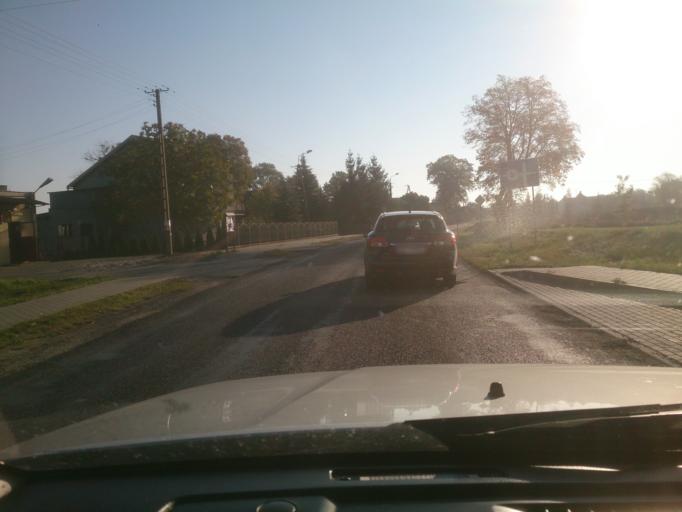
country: PL
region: Kujawsko-Pomorskie
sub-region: Powiat brodnicki
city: Brodnica
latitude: 53.2405
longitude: 19.4977
